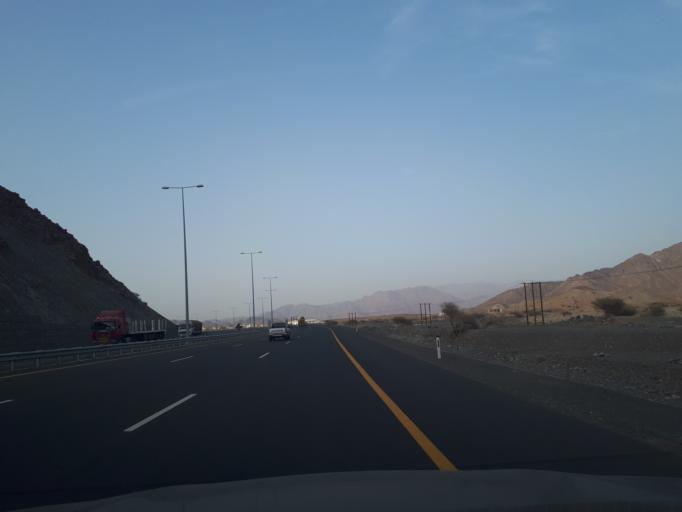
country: OM
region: Muhafazat ad Dakhiliyah
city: Bidbid
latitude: 23.3138
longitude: 58.1122
